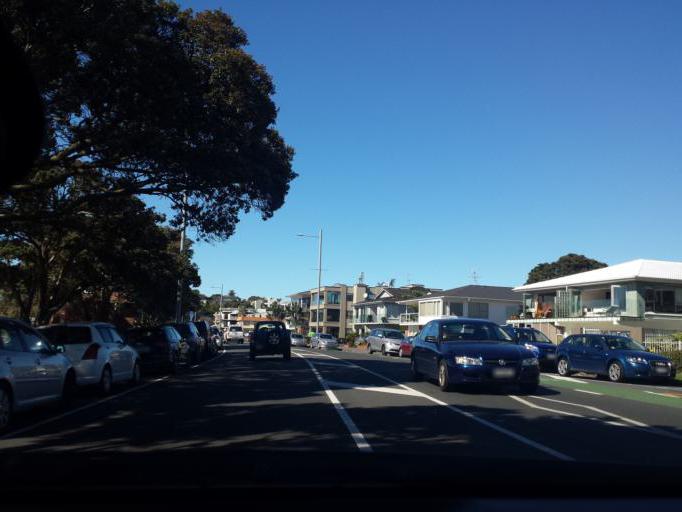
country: NZ
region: Auckland
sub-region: Auckland
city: Tamaki
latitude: -36.8499
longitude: 174.8426
